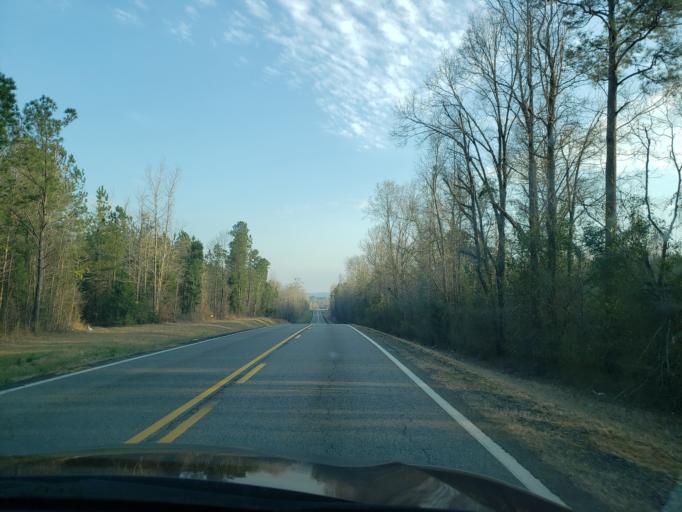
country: US
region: Alabama
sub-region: Hale County
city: Greensboro
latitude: 32.7838
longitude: -87.5887
